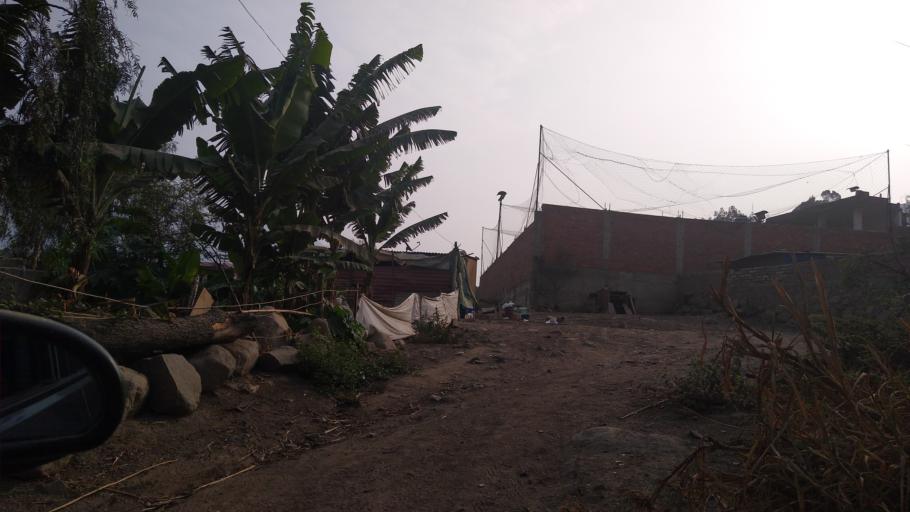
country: PE
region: Lima
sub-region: Provincia de Huarochiri
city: Santa Eulalia
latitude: -11.9071
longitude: -76.6656
